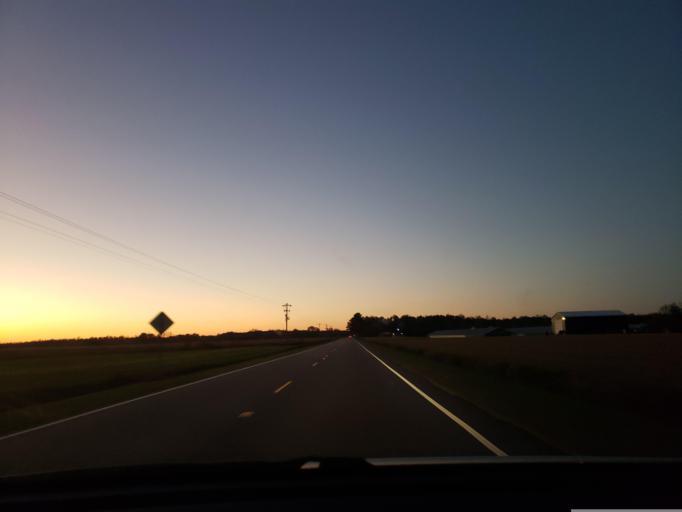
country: US
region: North Carolina
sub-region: Duplin County
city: Kenansville
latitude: 34.9050
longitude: -77.9209
